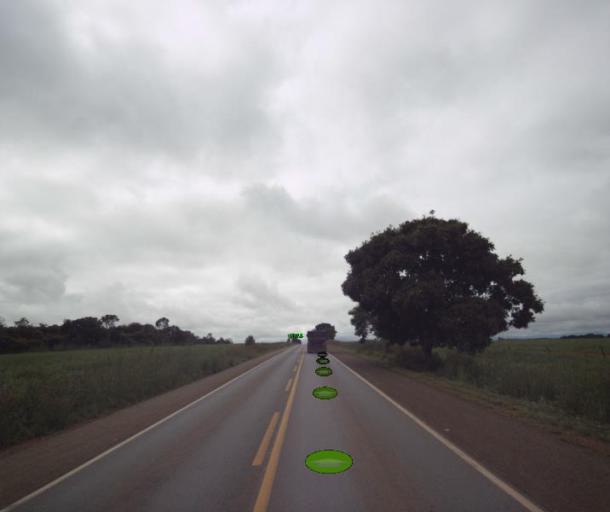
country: BR
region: Goias
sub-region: Uruacu
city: Uruacu
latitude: -14.6610
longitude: -49.1559
